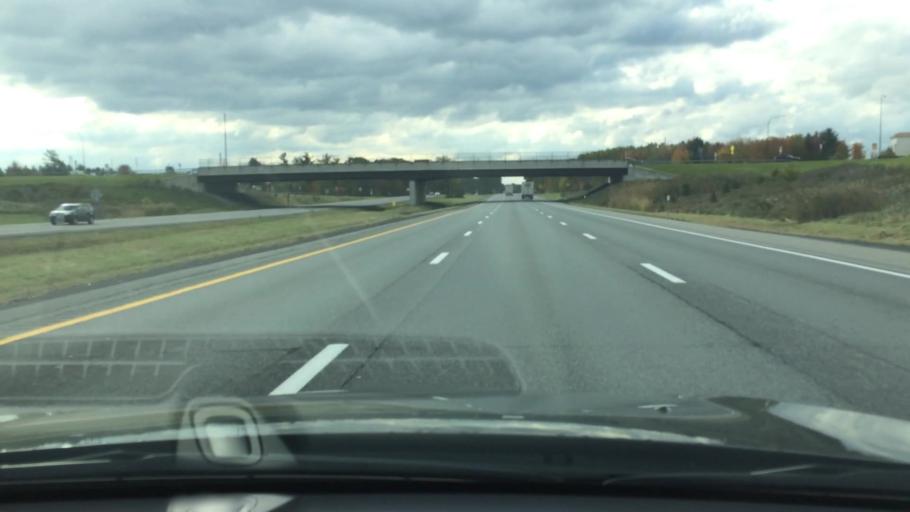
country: US
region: New York
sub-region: Saratoga County
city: Ballston Spa
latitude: 42.9719
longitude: -73.8023
